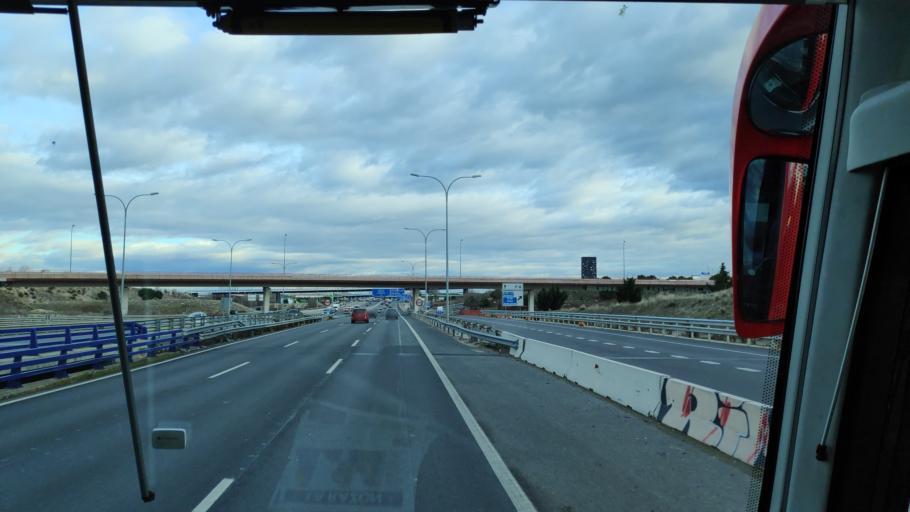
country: ES
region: Madrid
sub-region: Provincia de Madrid
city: Villa de Vallecas
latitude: 40.3735
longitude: -3.5972
